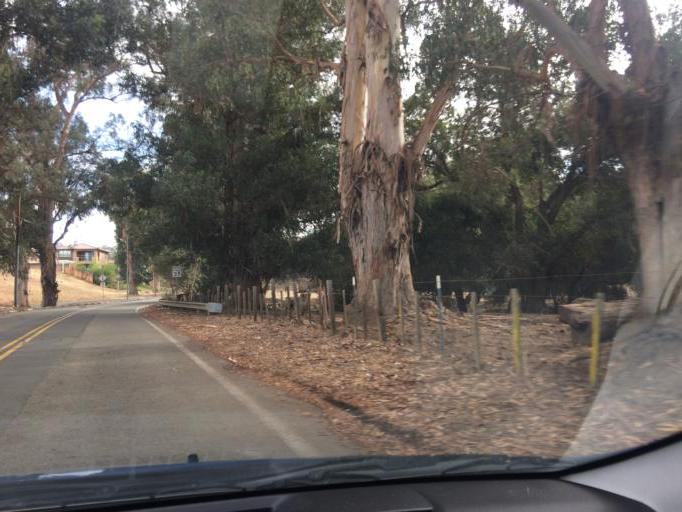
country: US
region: California
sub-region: Santa Clara County
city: Seven Trees
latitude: 37.2715
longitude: -121.7419
